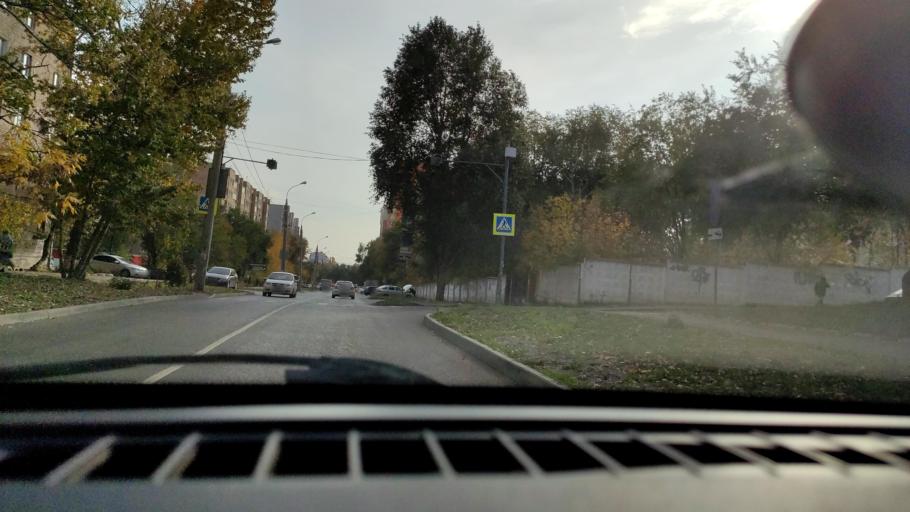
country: RU
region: Samara
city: Samara
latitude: 53.2105
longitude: 50.2206
